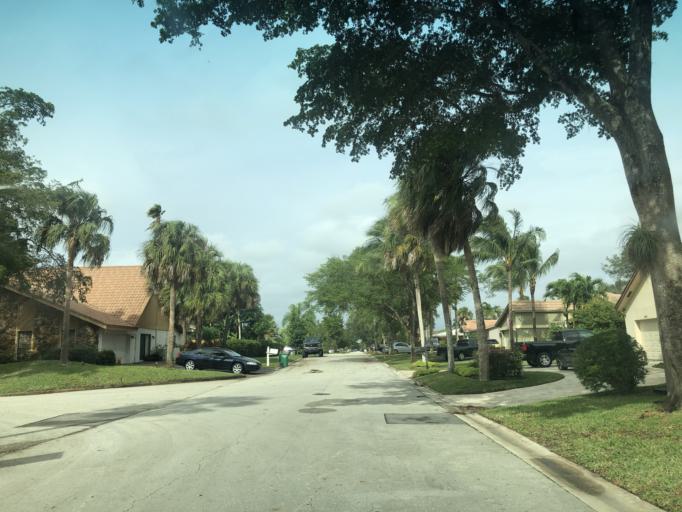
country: US
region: Florida
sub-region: Broward County
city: Margate
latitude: 26.2498
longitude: -80.2347
